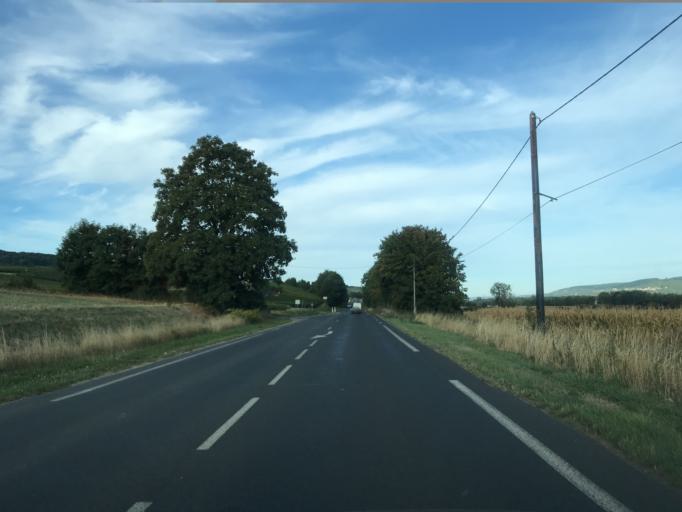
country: FR
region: Champagne-Ardenne
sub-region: Departement de la Marne
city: Mardeuil
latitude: 49.0522
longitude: 3.9165
